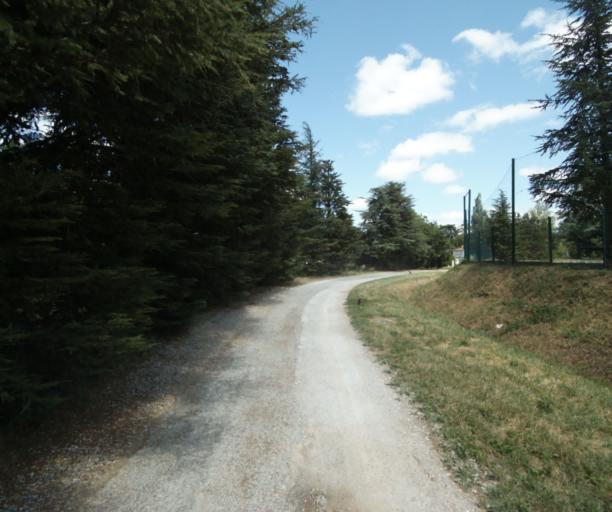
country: FR
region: Midi-Pyrenees
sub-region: Departement de la Haute-Garonne
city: Revel
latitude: 43.4530
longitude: 2.0124
